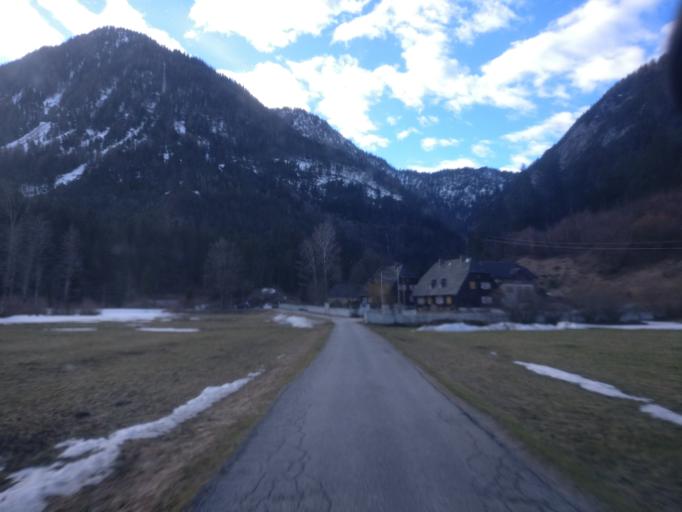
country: AT
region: Styria
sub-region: Politischer Bezirk Liezen
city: Sankt Martin am Grimming
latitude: 47.4897
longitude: 13.9608
